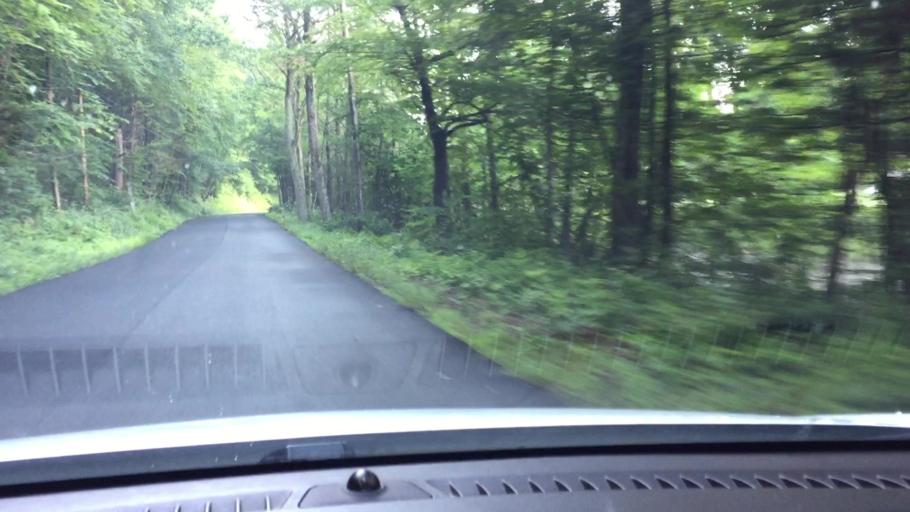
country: US
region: Massachusetts
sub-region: Hampshire County
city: Chesterfield
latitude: 42.3406
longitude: -72.9502
